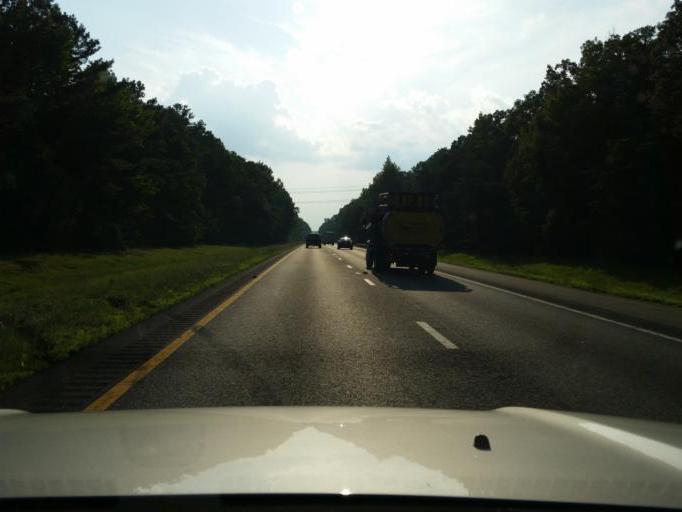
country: US
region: Virginia
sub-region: New Kent County
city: New Kent
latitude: 37.4945
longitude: -77.0143
